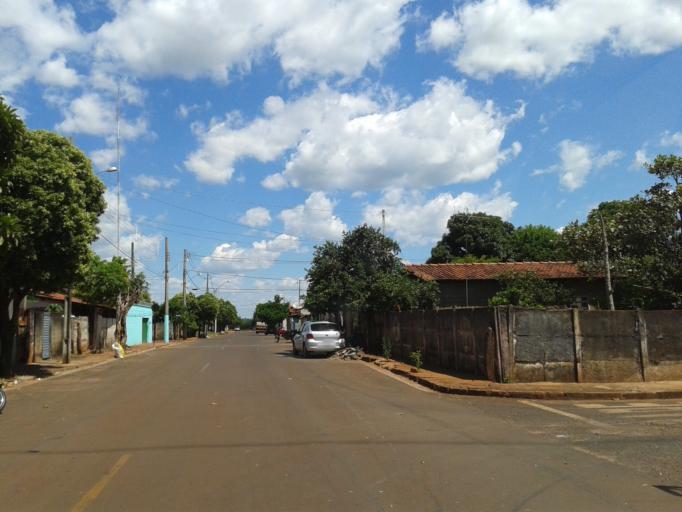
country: BR
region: Minas Gerais
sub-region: Centralina
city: Centralina
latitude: -18.7227
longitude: -49.1939
